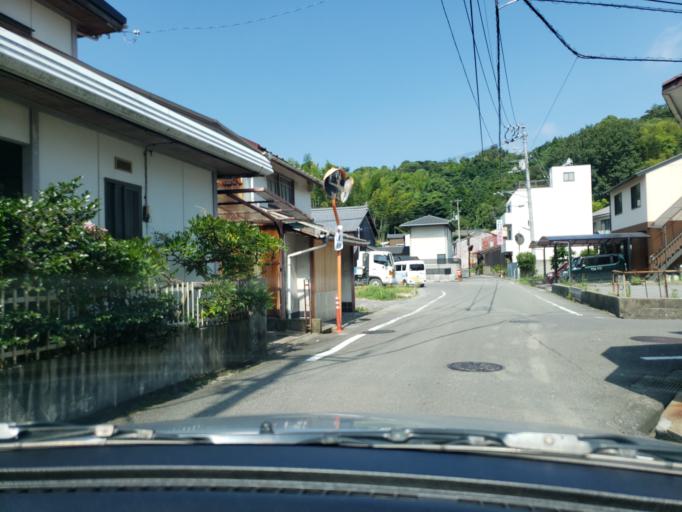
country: JP
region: Ehime
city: Hojo
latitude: 34.1076
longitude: 132.9681
